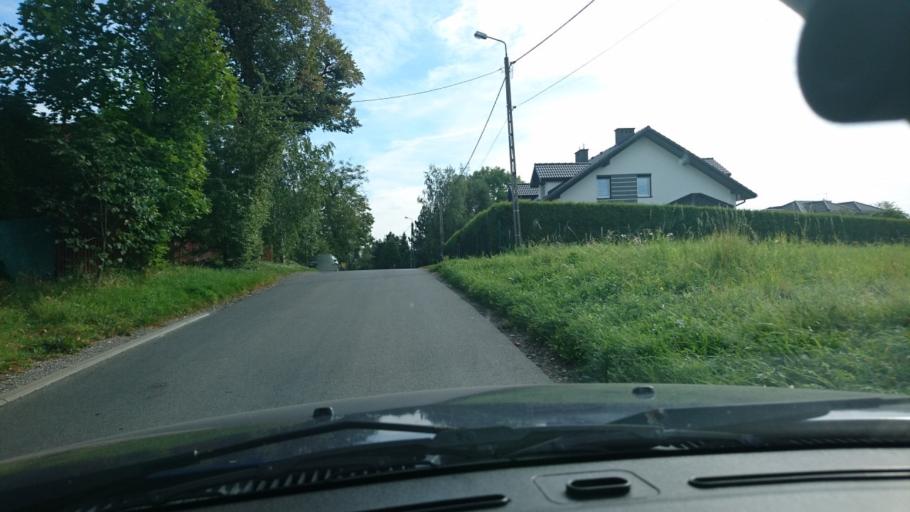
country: PL
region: Silesian Voivodeship
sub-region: Powiat bielski
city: Mazancowice
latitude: 49.8193
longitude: 18.9945
